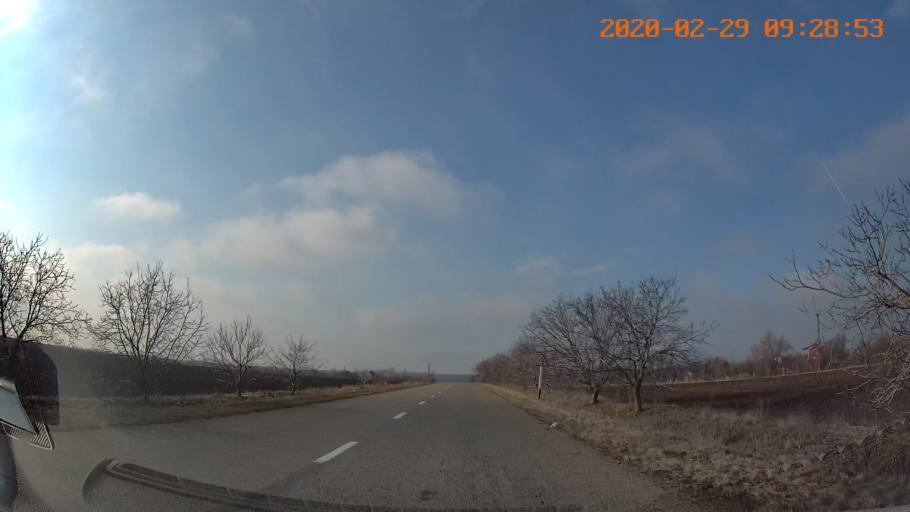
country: UA
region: Odessa
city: Lymanske
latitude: 46.6839
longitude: 29.9254
